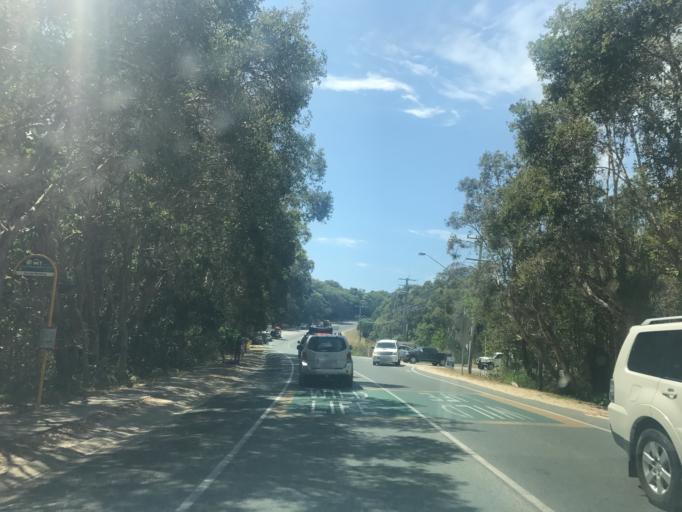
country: AU
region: Queensland
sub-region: Redland
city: Victoria Point
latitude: -27.4277
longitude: 153.5272
